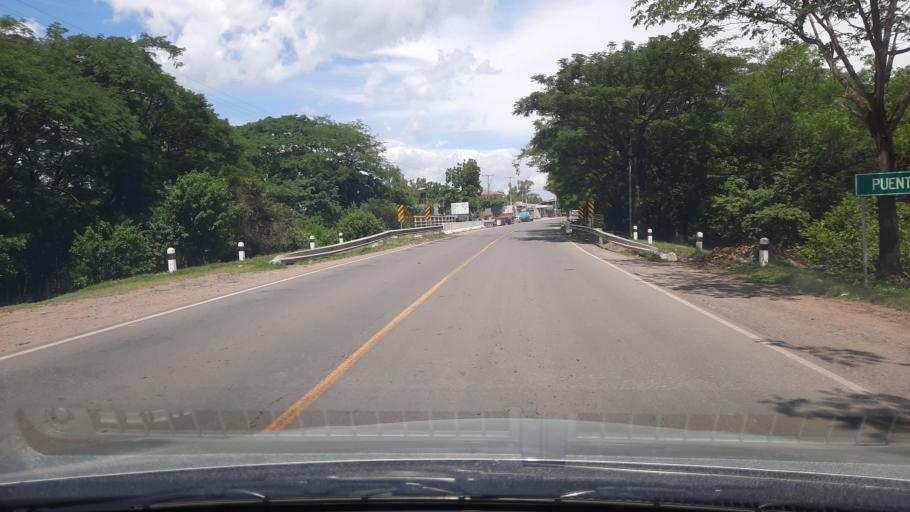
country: NI
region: Chinandega
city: Somotillo
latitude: 13.0491
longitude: -86.9050
